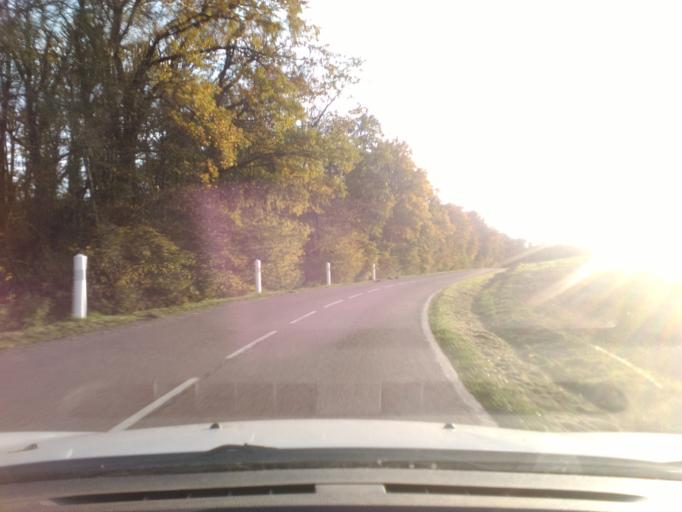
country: FR
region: Lorraine
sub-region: Departement des Vosges
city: Mirecourt
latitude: 48.2176
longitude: 6.1568
